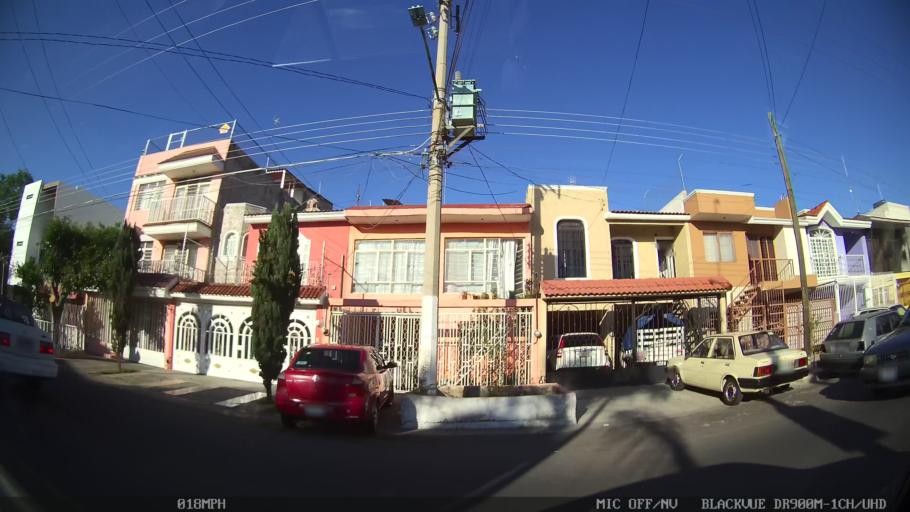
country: MX
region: Jalisco
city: Tlaquepaque
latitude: 20.7029
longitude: -103.2969
